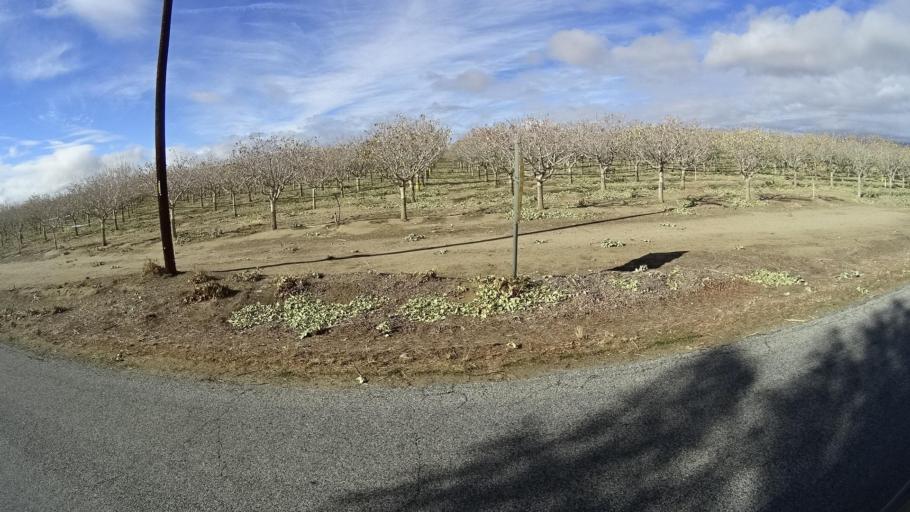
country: US
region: California
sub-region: Kern County
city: Rosamond
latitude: 34.8227
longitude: -118.3087
